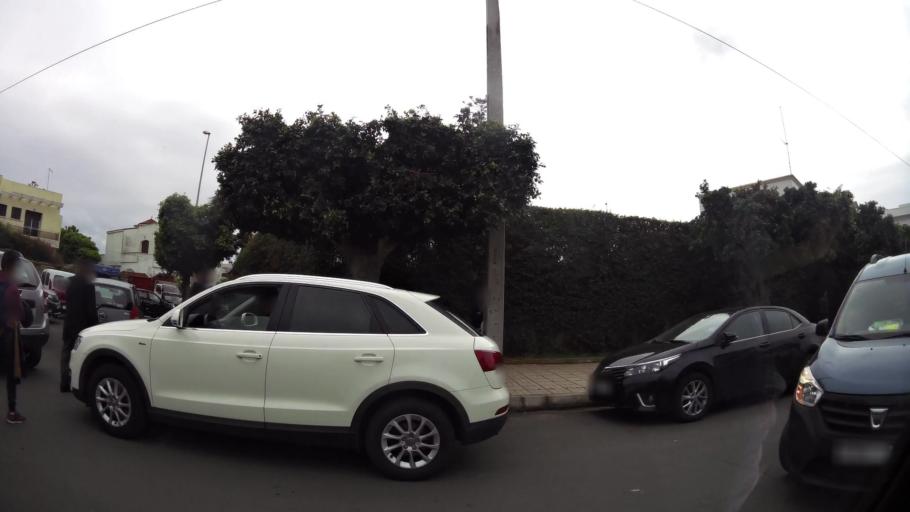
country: MA
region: Grand Casablanca
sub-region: Casablanca
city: Casablanca
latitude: 33.5940
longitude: -7.6499
